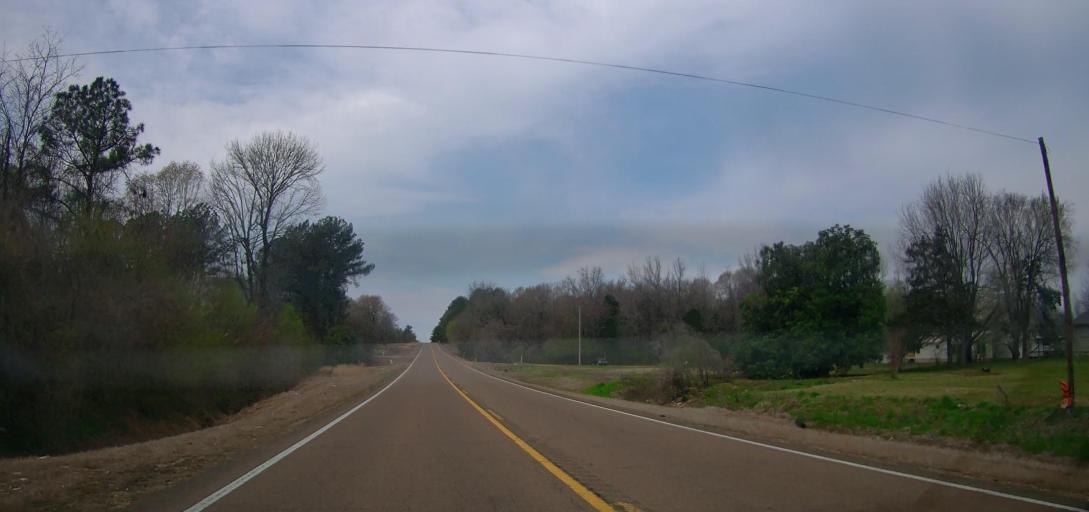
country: US
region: Mississippi
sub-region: Marshall County
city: Byhalia
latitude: 34.8374
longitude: -89.5919
